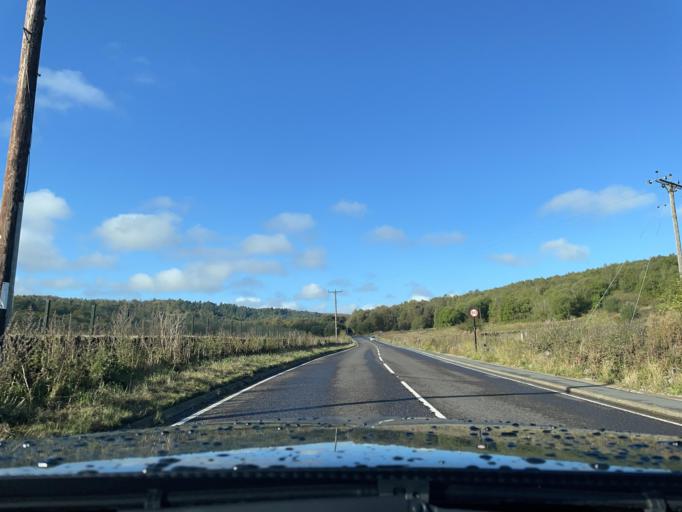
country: GB
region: England
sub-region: Sheffield
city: Bradfield
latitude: 53.3782
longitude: -1.5767
